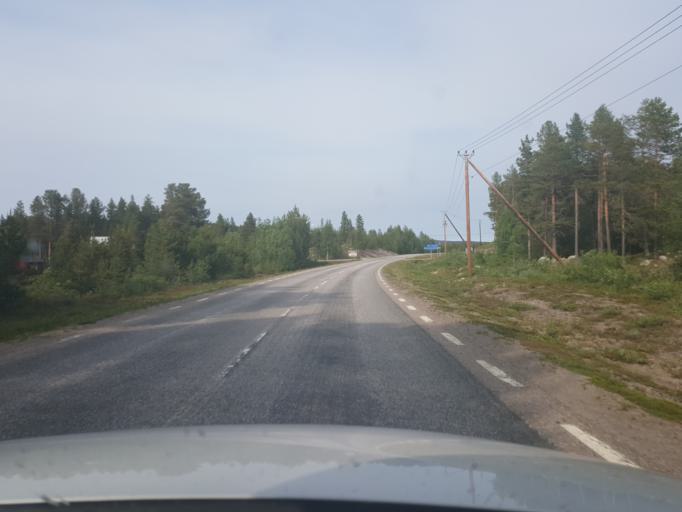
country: SE
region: Norrbotten
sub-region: Arjeplogs Kommun
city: Arjeplog
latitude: 65.8406
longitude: 18.0276
